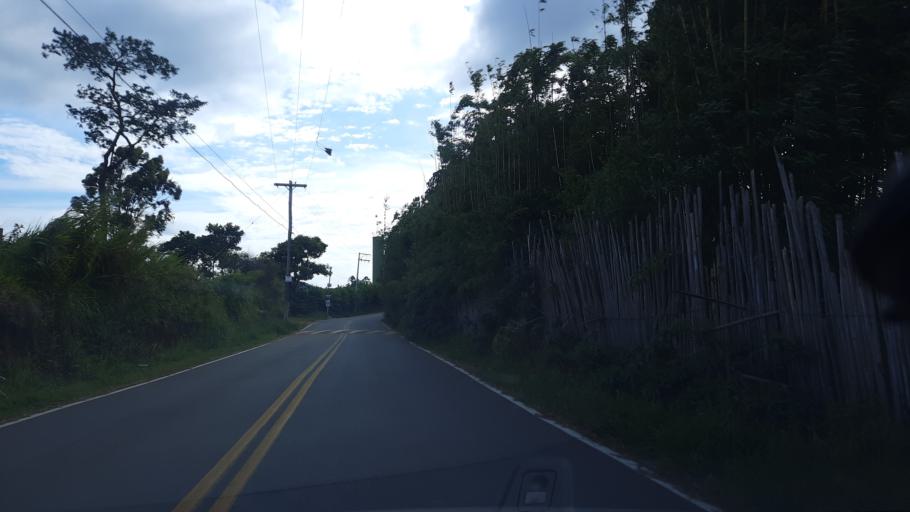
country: BR
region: Sao Paulo
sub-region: Atibaia
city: Atibaia
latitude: -23.0867
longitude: -46.5105
